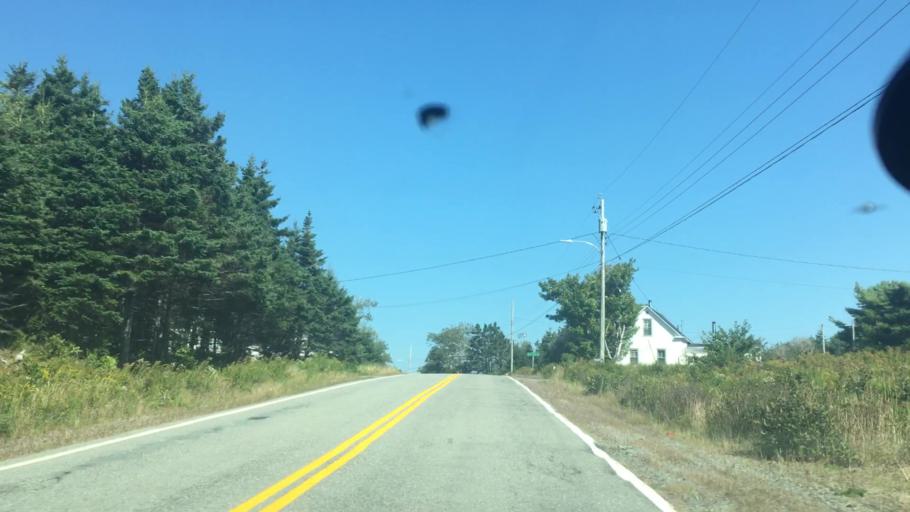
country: CA
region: Nova Scotia
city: New Glasgow
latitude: 44.9129
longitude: -62.3842
